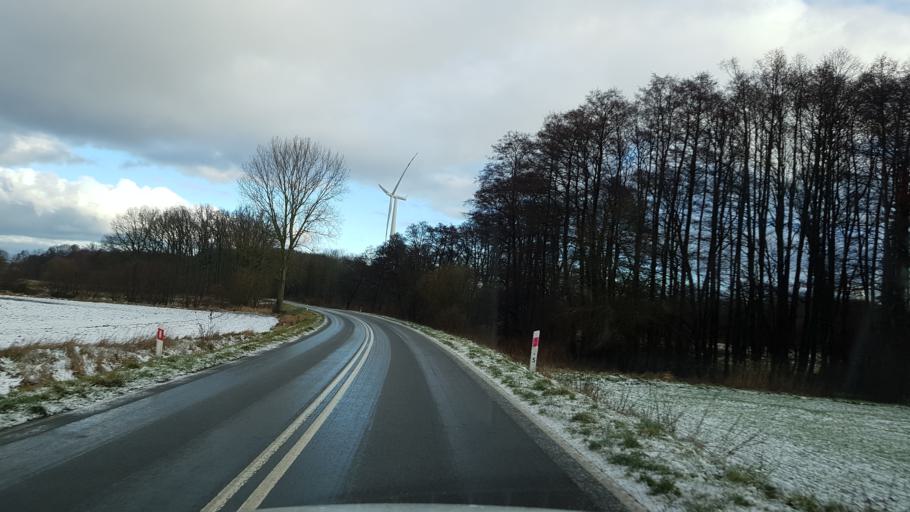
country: PL
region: West Pomeranian Voivodeship
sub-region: Powiat gryficki
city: Karnice
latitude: 54.0397
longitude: 15.0598
